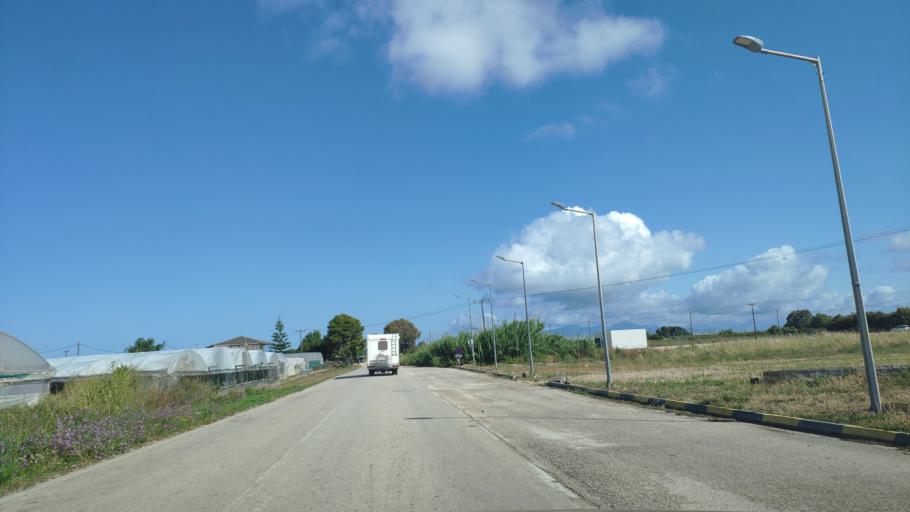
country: GR
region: Epirus
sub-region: Nomos Prevezis
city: Preveza
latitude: 38.9332
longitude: 20.7720
